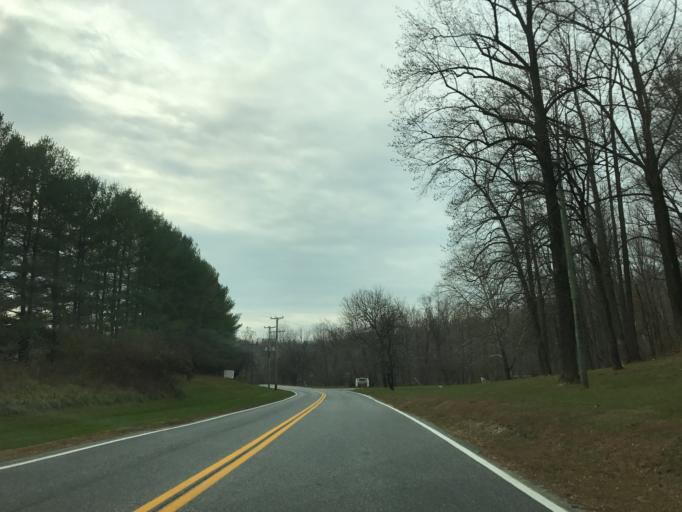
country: US
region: Maryland
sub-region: Baltimore County
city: Randallstown
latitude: 39.3680
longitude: -76.8744
